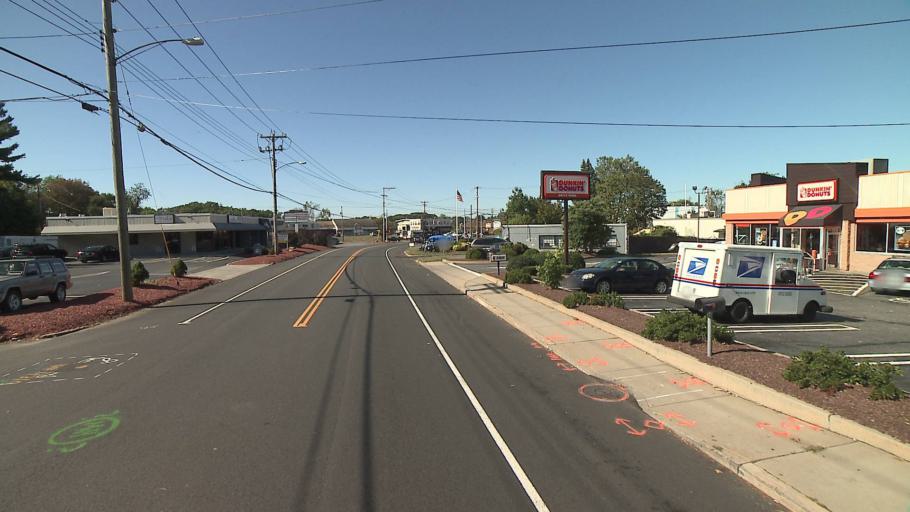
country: US
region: Connecticut
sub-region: New Haven County
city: Milford
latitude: 41.2255
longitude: -73.0288
